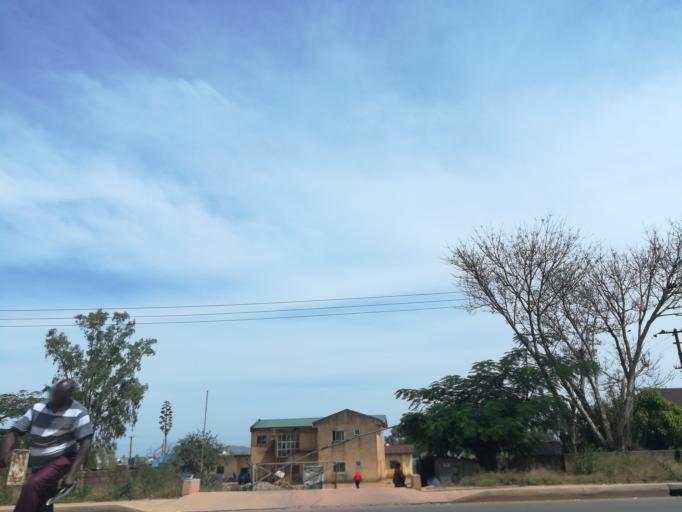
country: NG
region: Plateau
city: Bukuru
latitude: 9.7744
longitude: 8.8605
